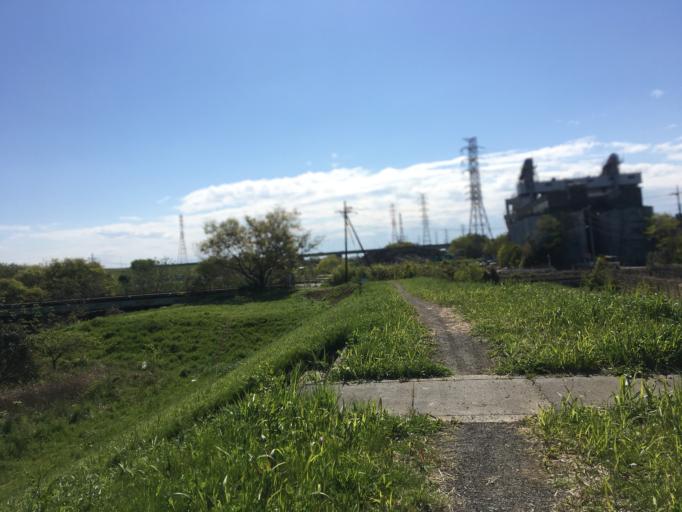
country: JP
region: Saitama
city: Asaka
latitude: 35.8110
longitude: 139.6161
